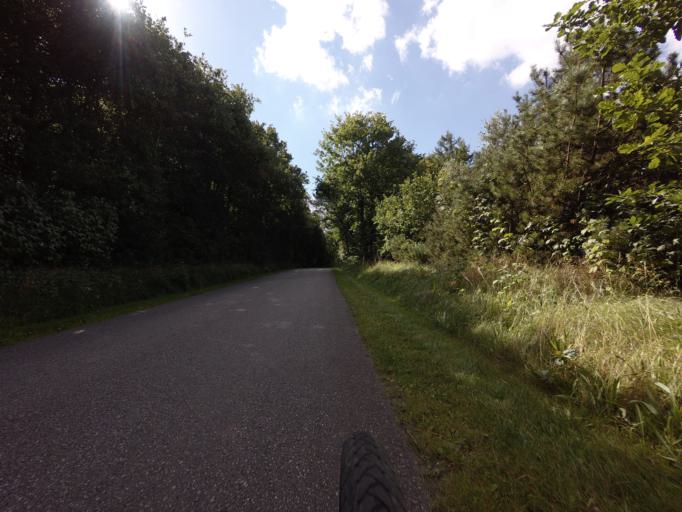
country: DK
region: Central Jutland
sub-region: Ikast-Brande Kommune
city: Brande
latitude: 55.9770
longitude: 9.1648
